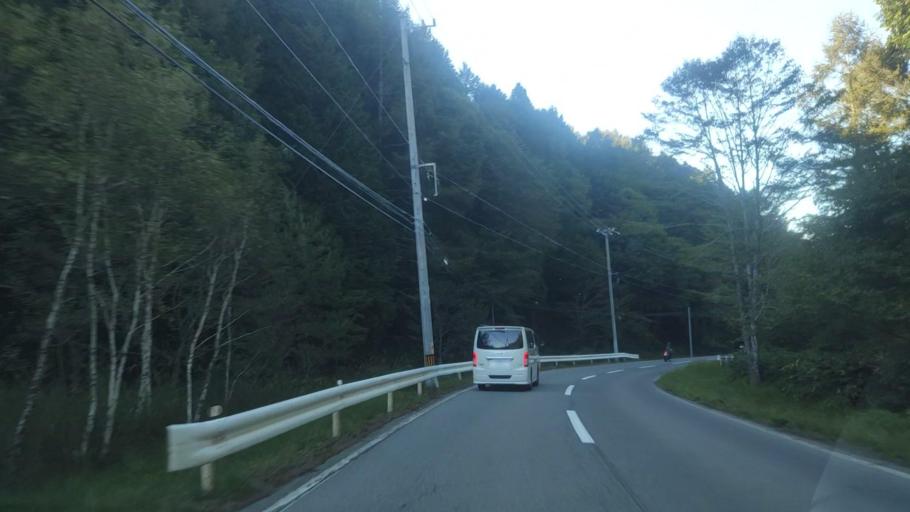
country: JP
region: Nagano
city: Kamimaruko
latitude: 36.2189
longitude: 138.2932
